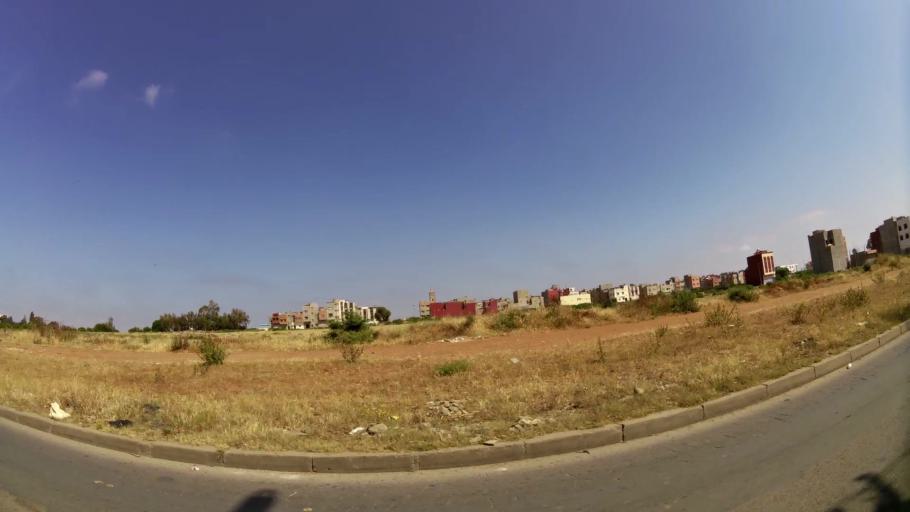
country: MA
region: Rabat-Sale-Zemmour-Zaer
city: Sale
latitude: 34.0780
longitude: -6.7594
